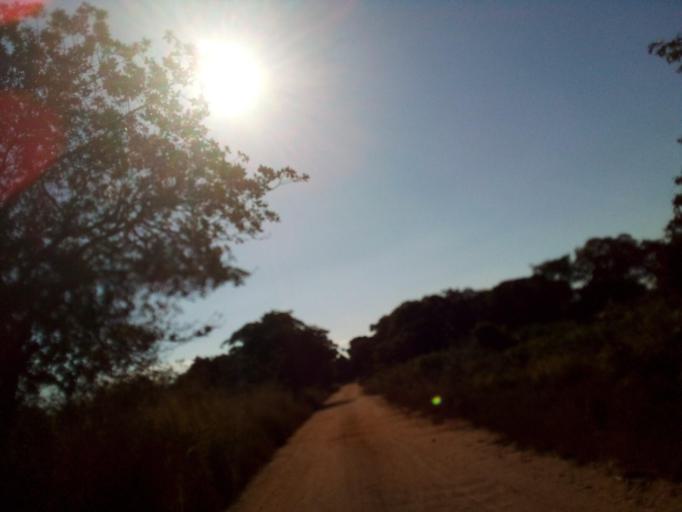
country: MZ
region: Zambezia
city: Quelimane
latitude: -17.5068
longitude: 36.5890
